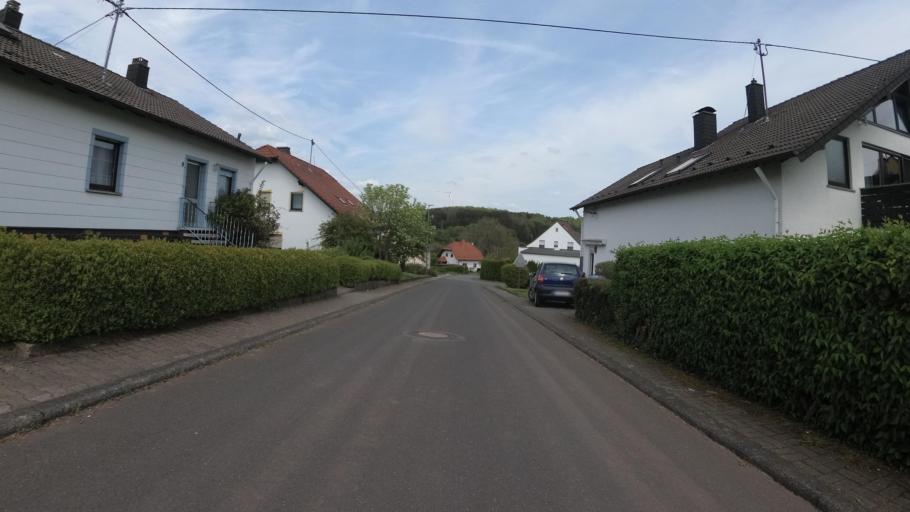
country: DE
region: Rheinland-Pfalz
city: Fohren-Linden
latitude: 49.5857
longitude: 7.2885
